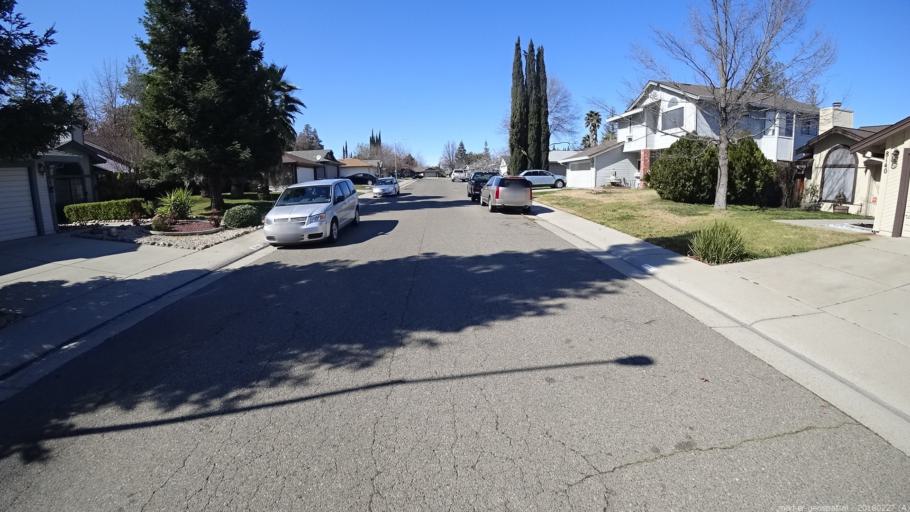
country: US
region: California
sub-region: Sacramento County
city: North Highlands
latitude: 38.7177
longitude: -121.3752
